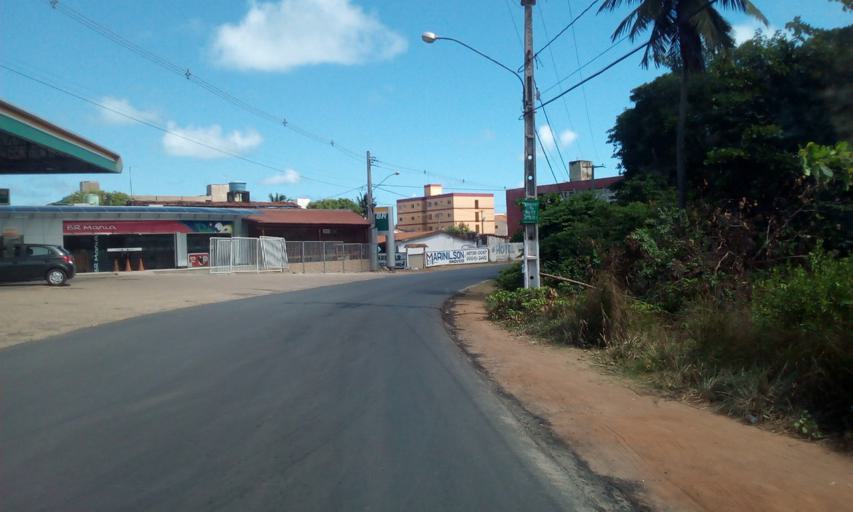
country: BR
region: Paraiba
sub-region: Conde
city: Conde
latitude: -7.2783
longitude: -34.8013
